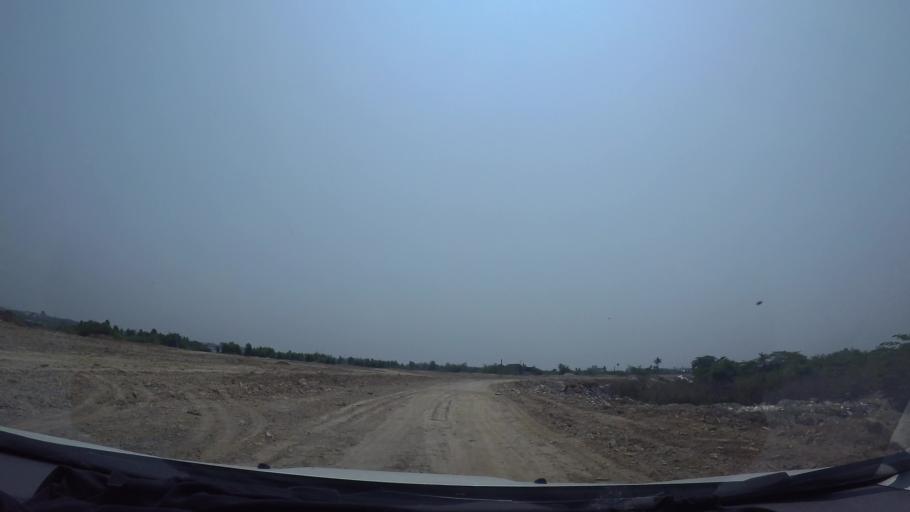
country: VN
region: Da Nang
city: Cam Le
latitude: 15.9950
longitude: 108.2246
